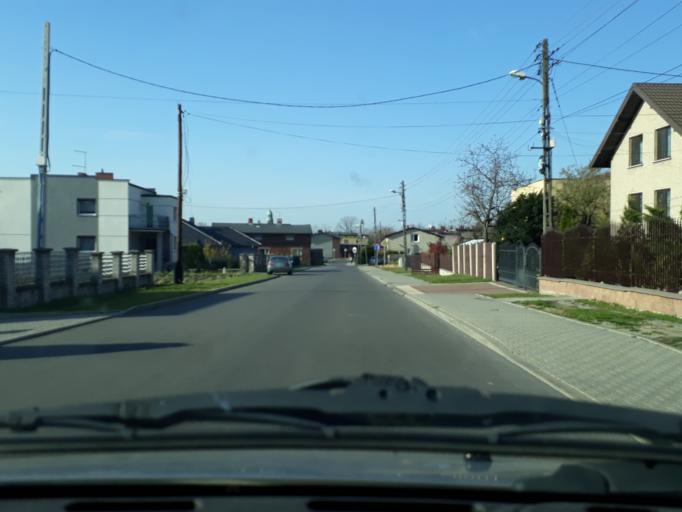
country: PL
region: Silesian Voivodeship
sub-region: Powiat tarnogorski
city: Tarnowskie Gory
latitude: 50.4225
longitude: 18.8790
